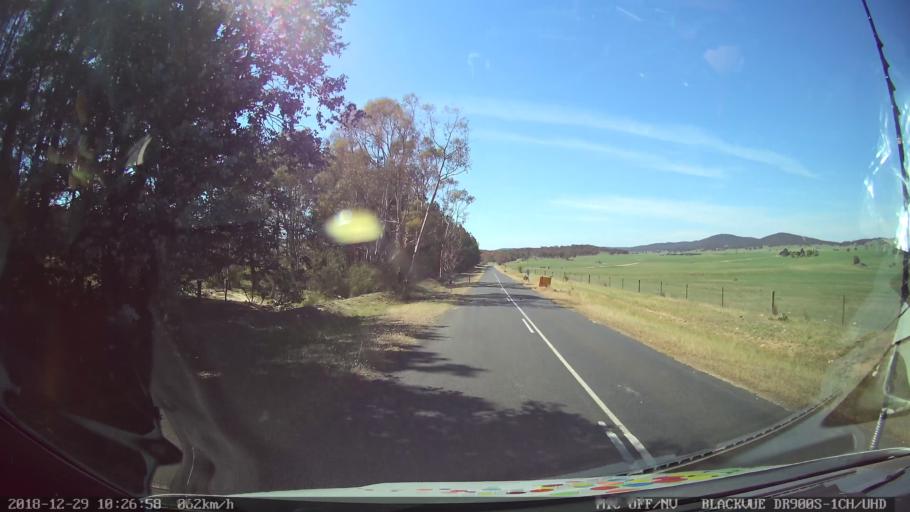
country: AU
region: New South Wales
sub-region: Yass Valley
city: Gundaroo
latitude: -34.9295
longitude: 149.4473
